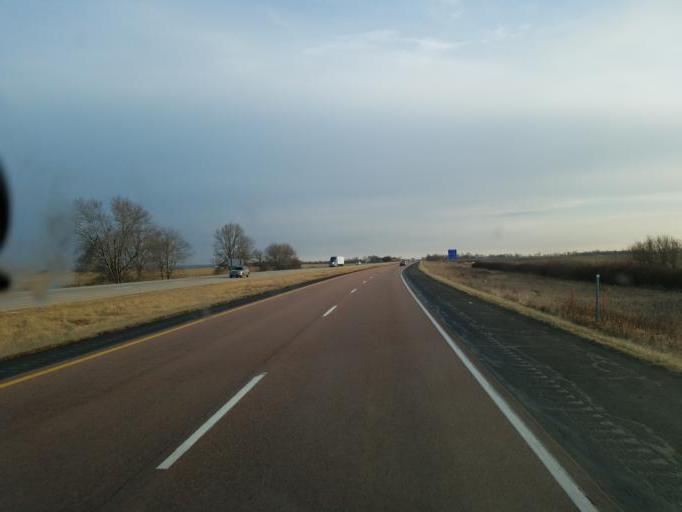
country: US
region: Iowa
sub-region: Monona County
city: Onawa
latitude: 42.0085
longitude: -96.1179
